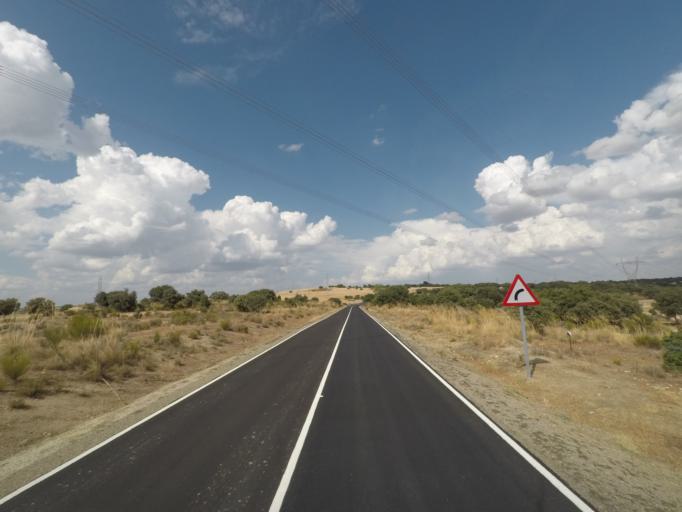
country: ES
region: Castille and Leon
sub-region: Provincia de Salamanca
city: Almendra
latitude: 41.2934
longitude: -6.3317
